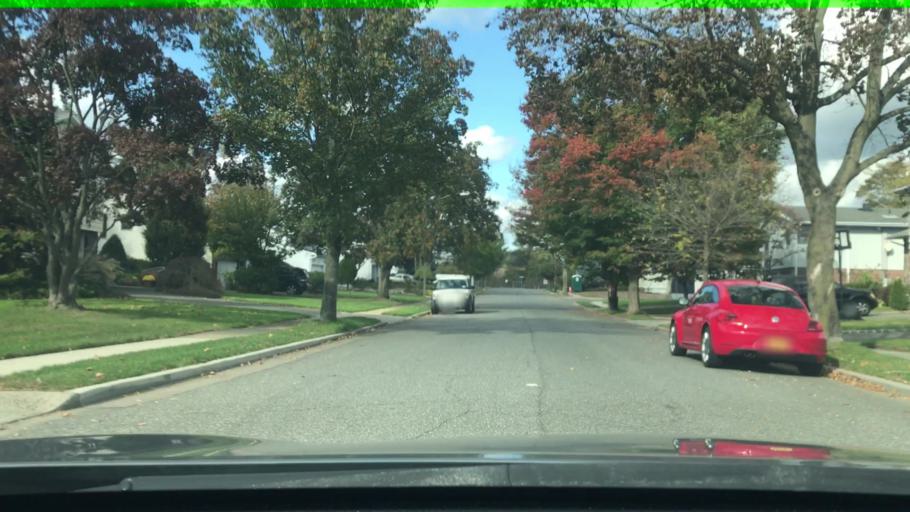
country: US
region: New York
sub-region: Nassau County
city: Jericho
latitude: 40.7816
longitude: -73.5435
